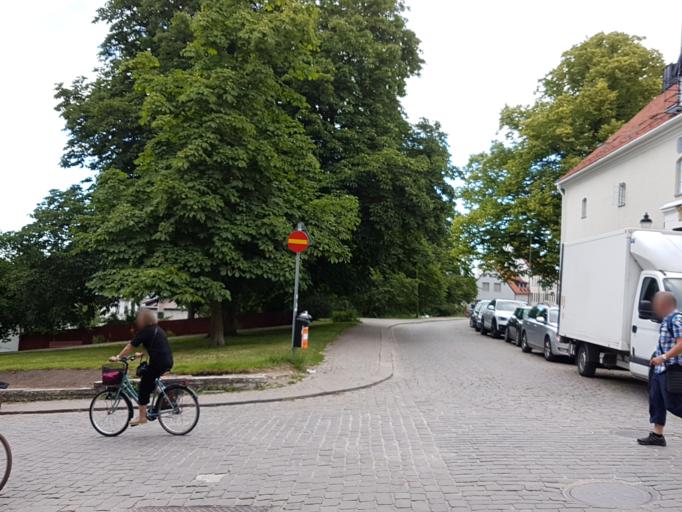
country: SE
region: Gotland
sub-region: Gotland
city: Visby
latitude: 57.6362
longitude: 18.2890
